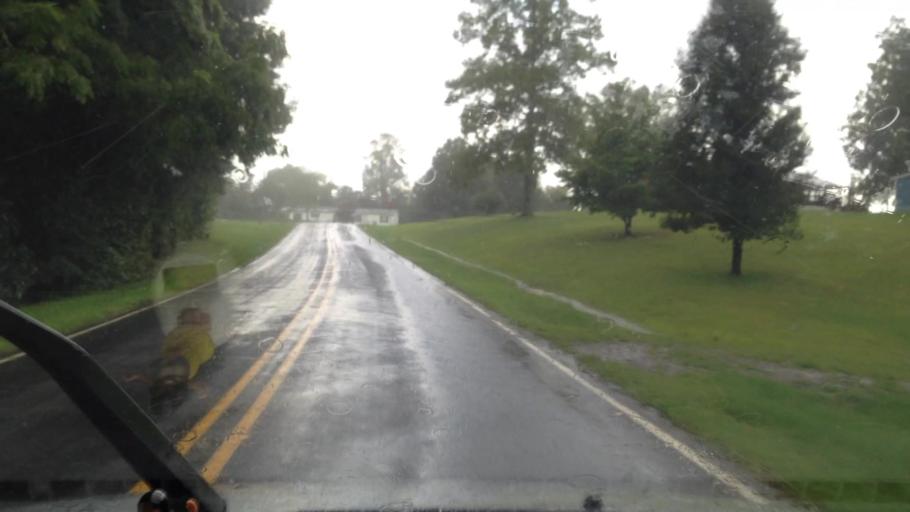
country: US
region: North Carolina
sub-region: Guilford County
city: Oak Ridge
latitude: 36.2084
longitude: -80.0251
